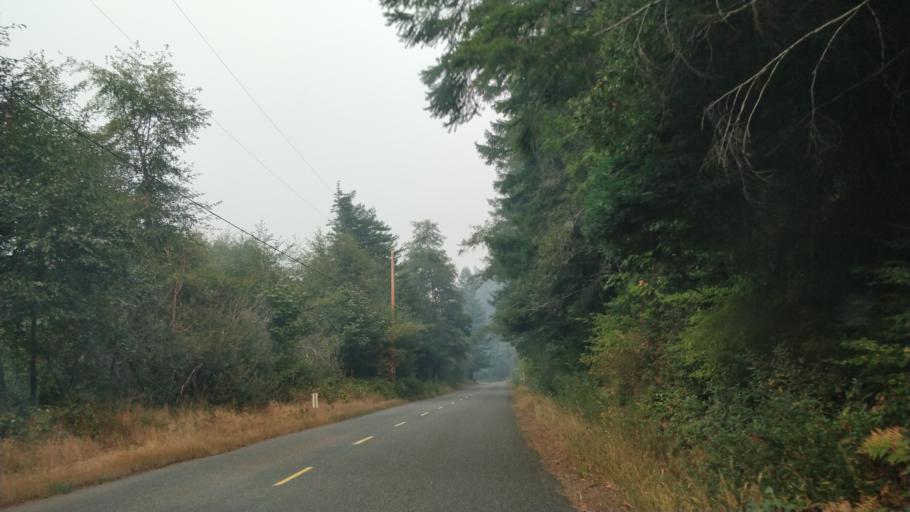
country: US
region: California
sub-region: Humboldt County
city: Rio Dell
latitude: 40.3490
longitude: -124.0218
